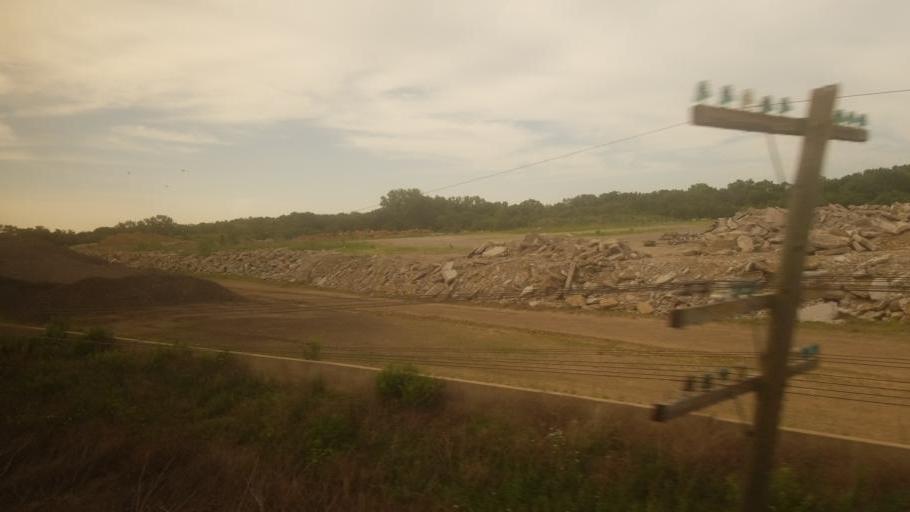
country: US
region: Kansas
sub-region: Shawnee County
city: Topeka
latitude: 39.0557
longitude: -95.6209
